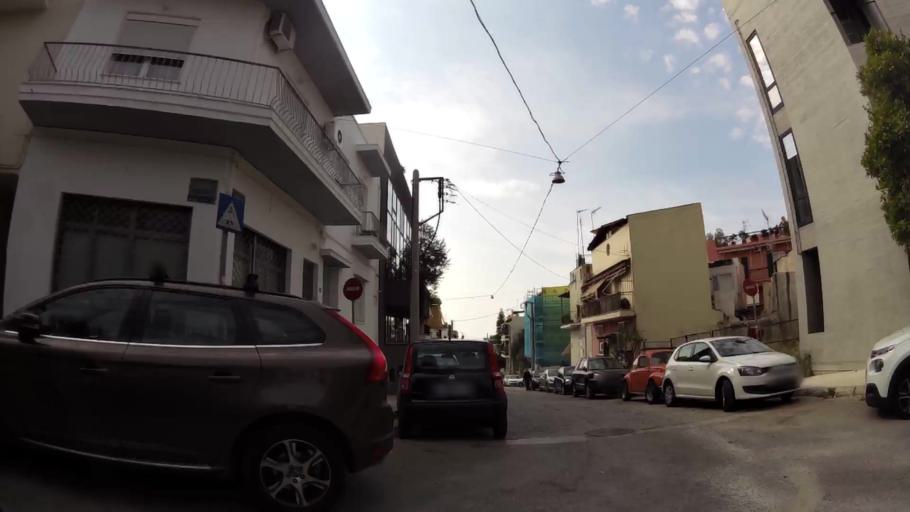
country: GR
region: Attica
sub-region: Nomarchia Athinas
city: Athens
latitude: 37.9667
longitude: 23.7144
